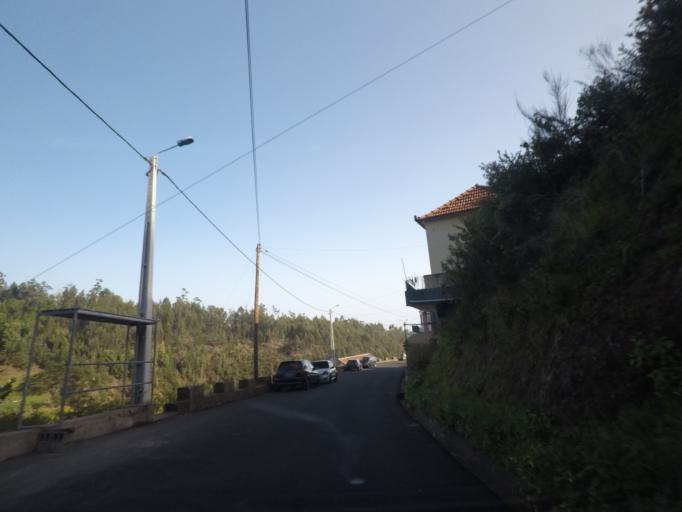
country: PT
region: Madeira
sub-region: Ribeira Brava
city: Campanario
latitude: 32.6760
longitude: -17.0060
